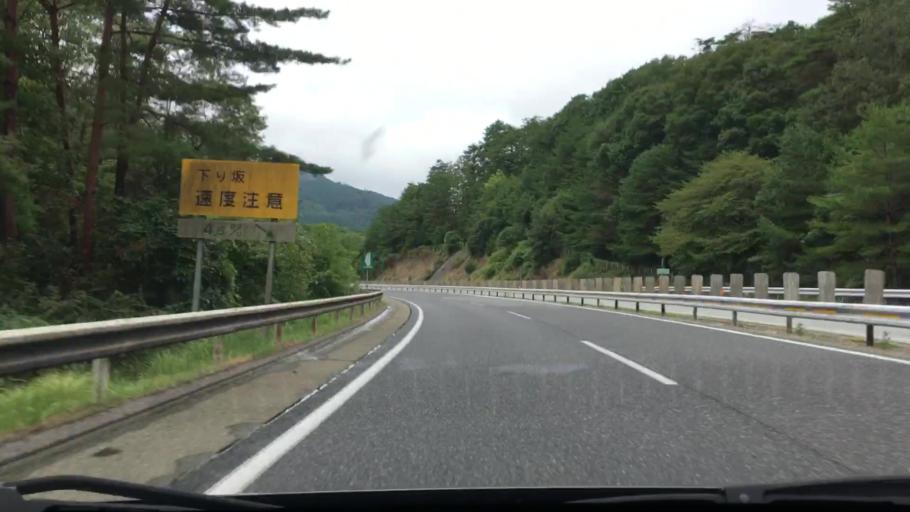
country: JP
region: Hiroshima
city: Shobara
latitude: 34.8603
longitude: 133.1016
